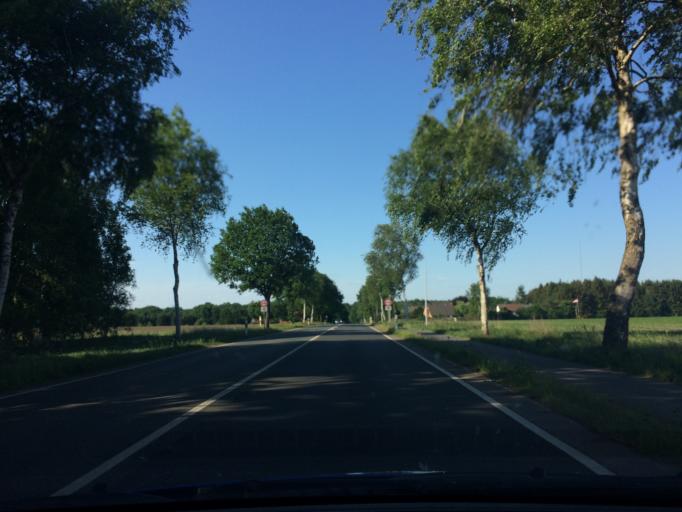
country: DE
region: Lower Saxony
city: Soltau
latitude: 53.0053
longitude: 9.8411
